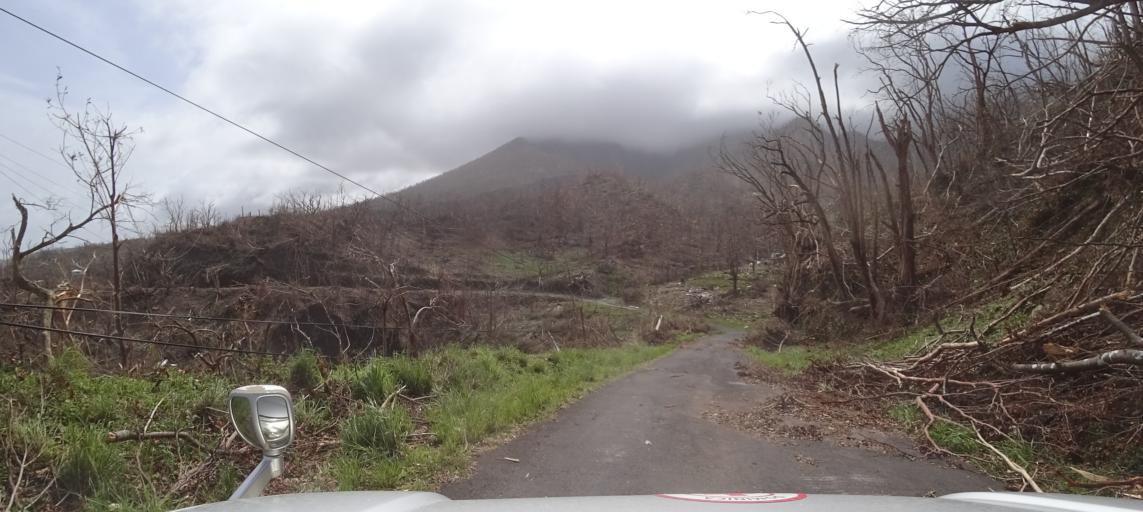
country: DM
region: Saint Patrick
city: La Plaine
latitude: 15.3152
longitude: -61.2485
